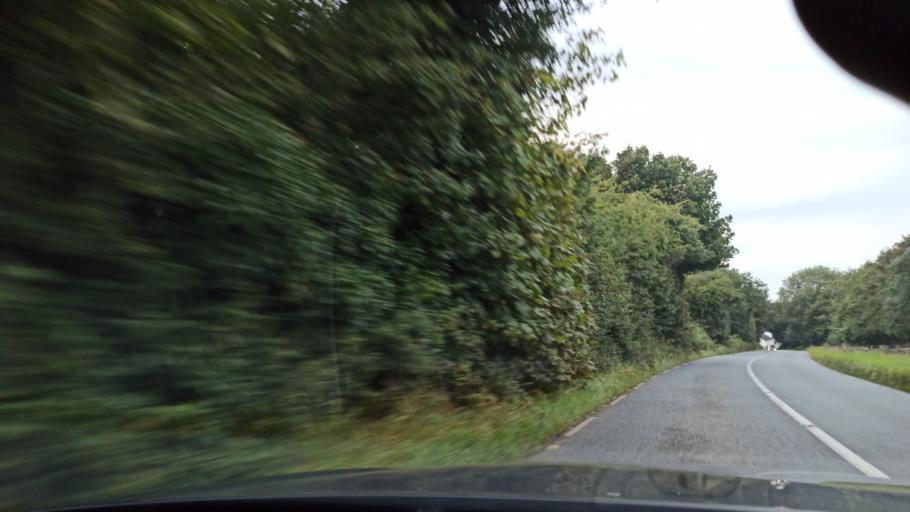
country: IE
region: Munster
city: Cashel
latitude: 52.4756
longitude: -7.8463
